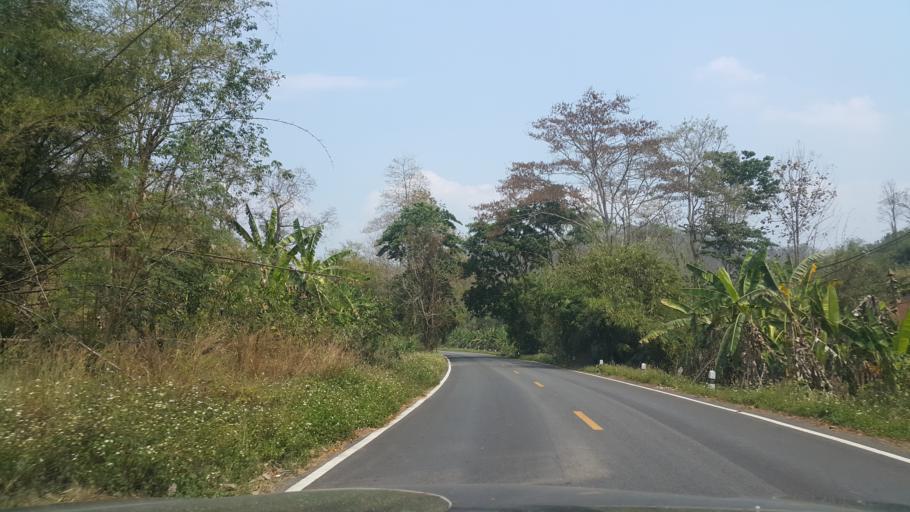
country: TH
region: Lamphun
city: Thung Hua Chang
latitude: 17.9012
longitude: 99.1331
